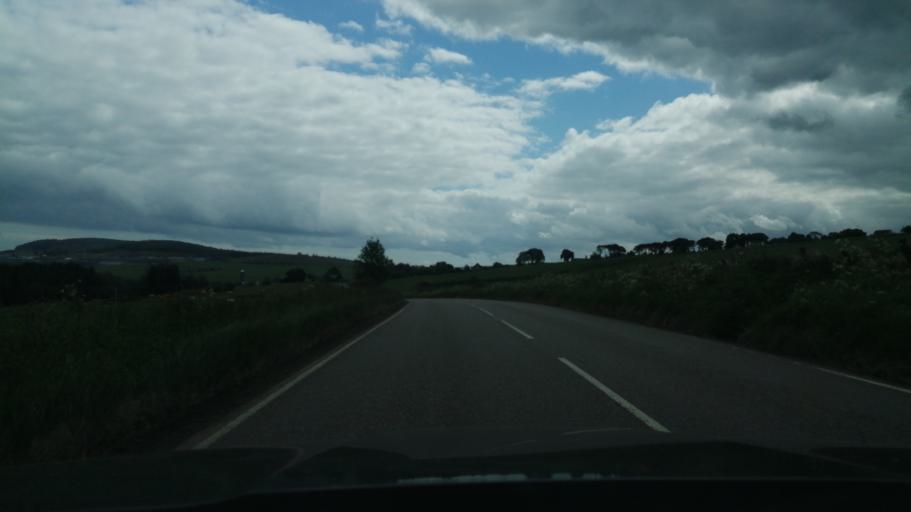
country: GB
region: Scotland
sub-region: Moray
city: Fochabers
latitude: 57.5474
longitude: -3.1049
